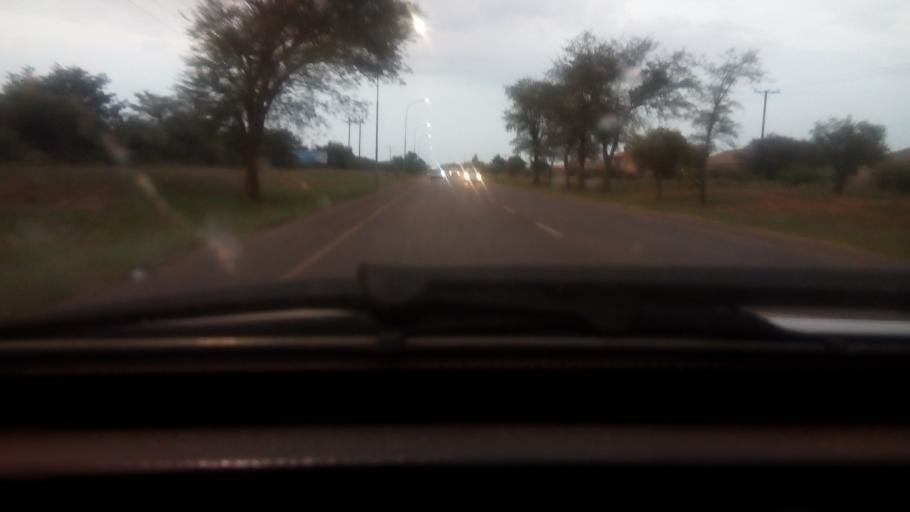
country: BW
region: South East
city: Gaborone
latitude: -24.5998
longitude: 25.9213
